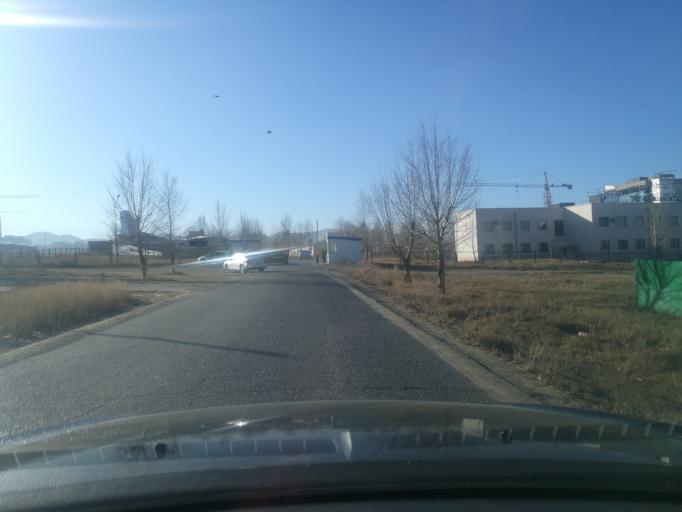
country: MN
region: Ulaanbaatar
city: Ulaanbaatar
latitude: 47.8536
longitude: 106.7800
